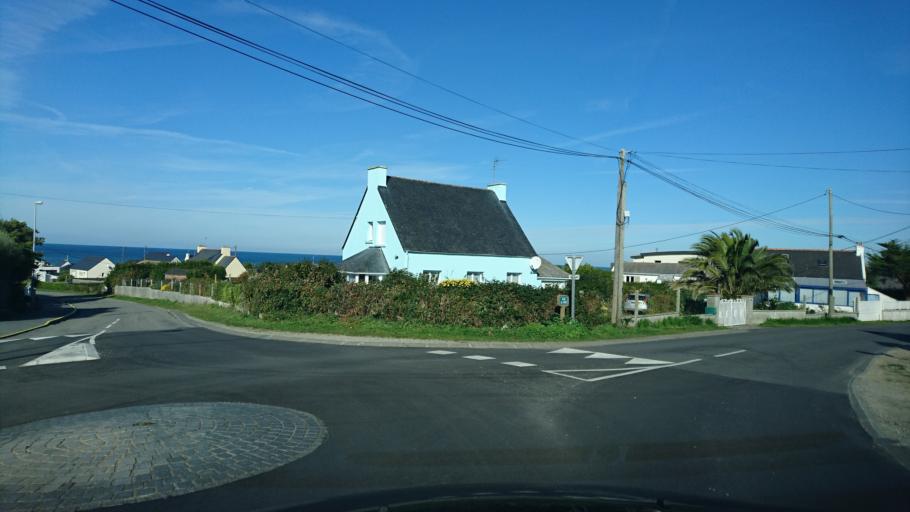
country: FR
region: Brittany
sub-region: Departement du Finistere
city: Lampaul-Plouarzel
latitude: 48.4360
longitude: -4.7745
